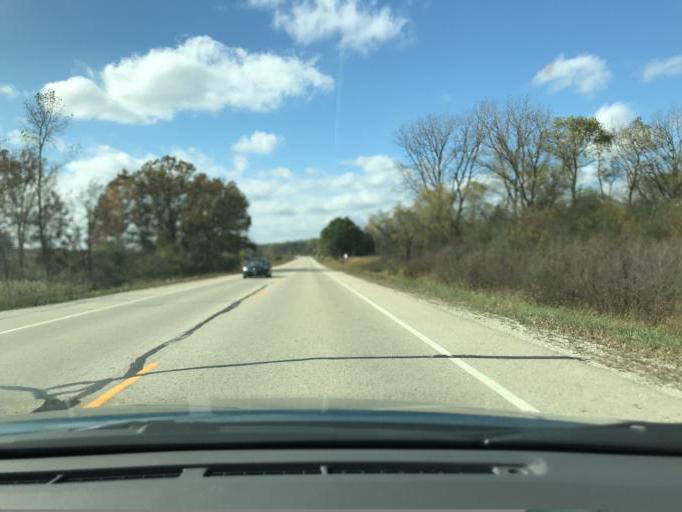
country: US
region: Wisconsin
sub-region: Racine County
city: Eagle Lake
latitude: 42.6366
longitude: -88.1505
